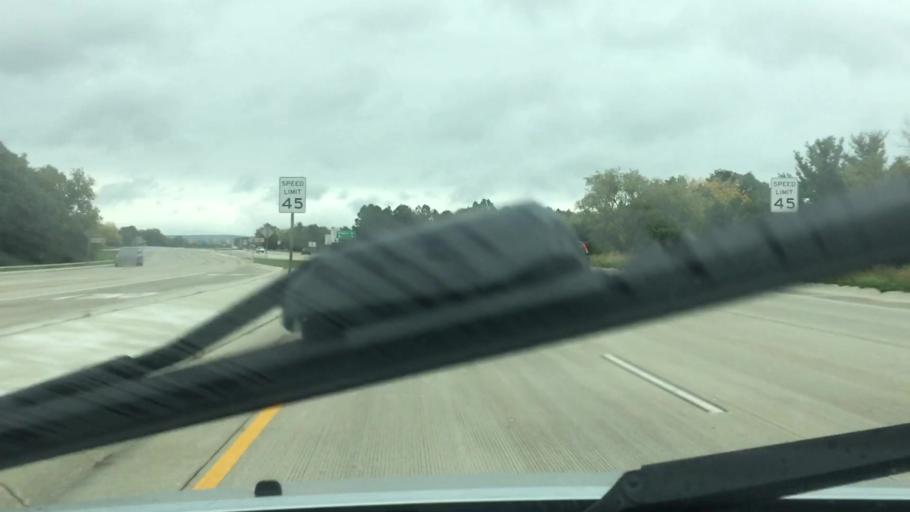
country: US
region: Wisconsin
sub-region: Waukesha County
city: Oconomowoc
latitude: 43.0919
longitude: -88.4770
